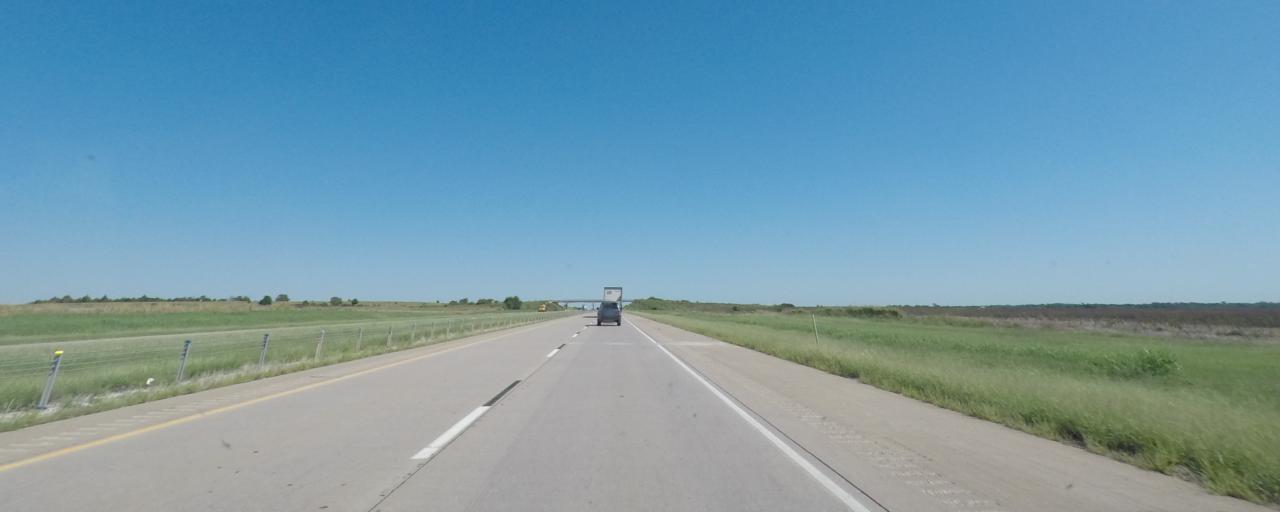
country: US
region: Oklahoma
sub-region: Noble County
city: Perry
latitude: 36.4448
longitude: -97.3269
